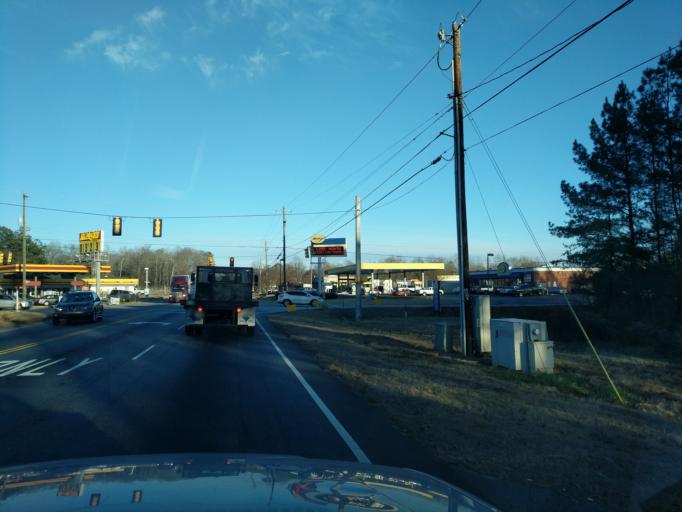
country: US
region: South Carolina
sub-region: Greenville County
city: Fountain Inn
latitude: 34.6617
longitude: -82.2639
